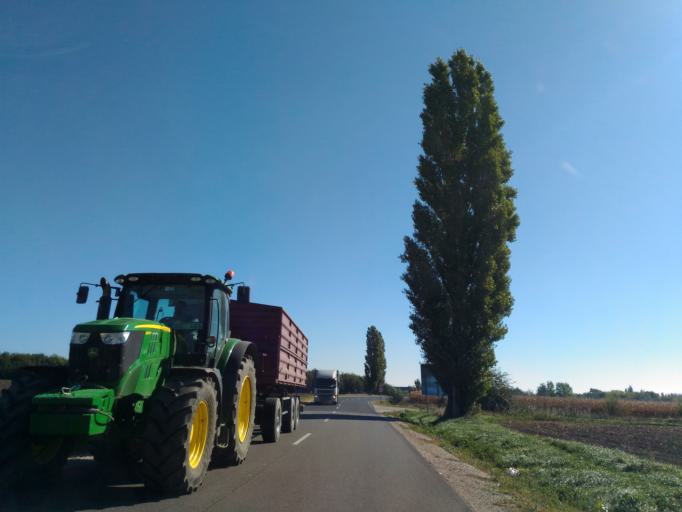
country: HU
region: Fejer
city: Ivancsa
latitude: 47.1331
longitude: 18.8113
